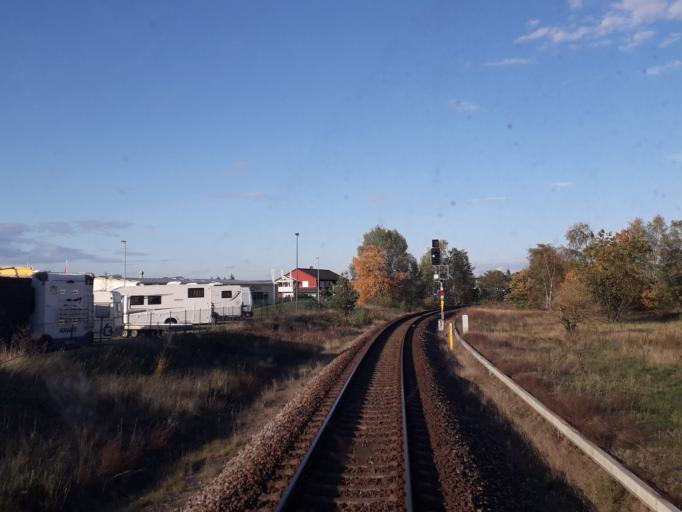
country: DE
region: Brandenburg
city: Perleberg
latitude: 53.0657
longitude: 11.8425
